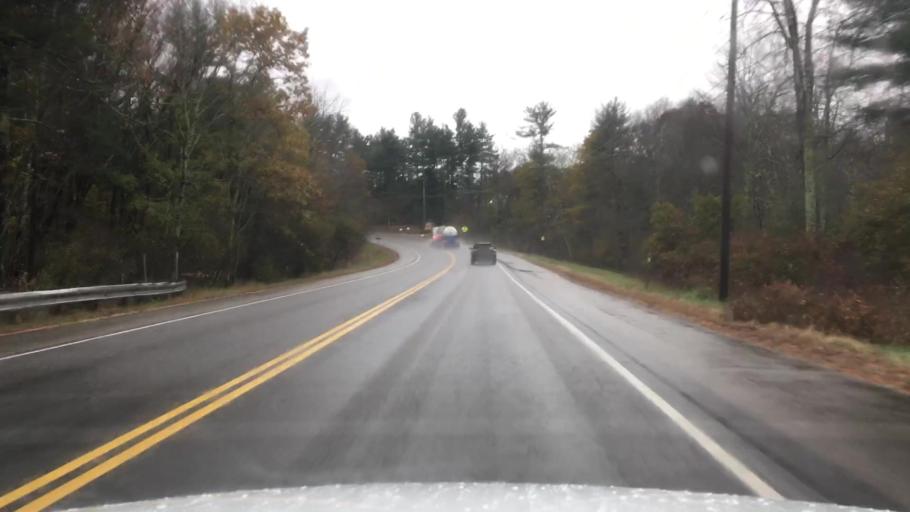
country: US
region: New Hampshire
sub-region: Strafford County
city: Barrington
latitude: 43.2329
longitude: -70.9923
